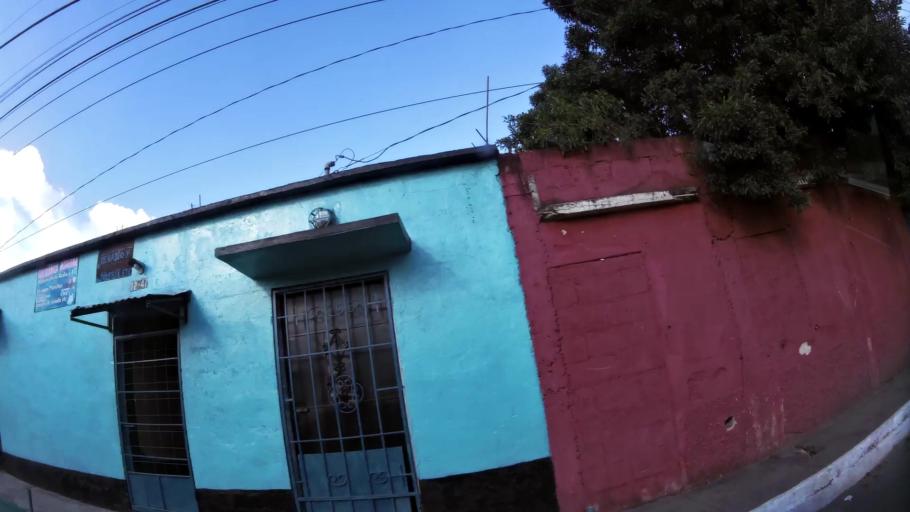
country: GT
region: Guatemala
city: Villa Nueva
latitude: 14.5214
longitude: -90.5813
